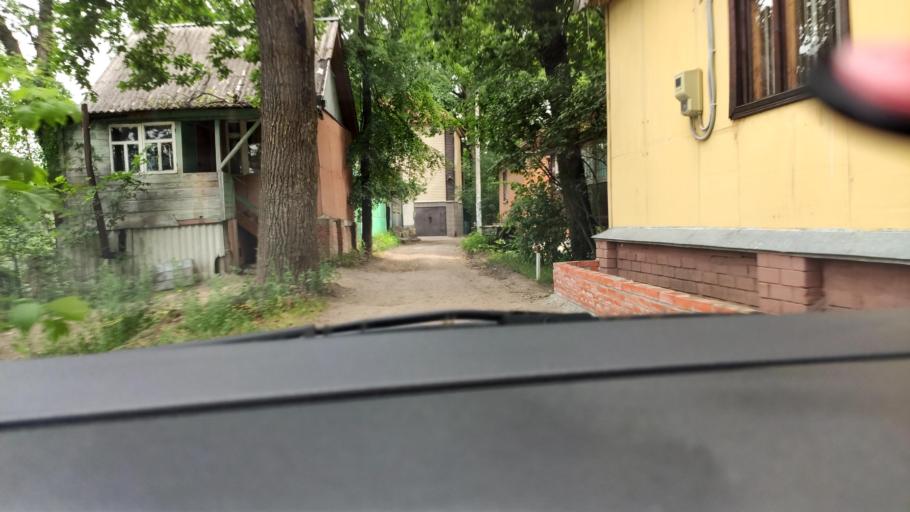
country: RU
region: Voronezj
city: Ramon'
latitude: 51.8875
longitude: 39.3469
